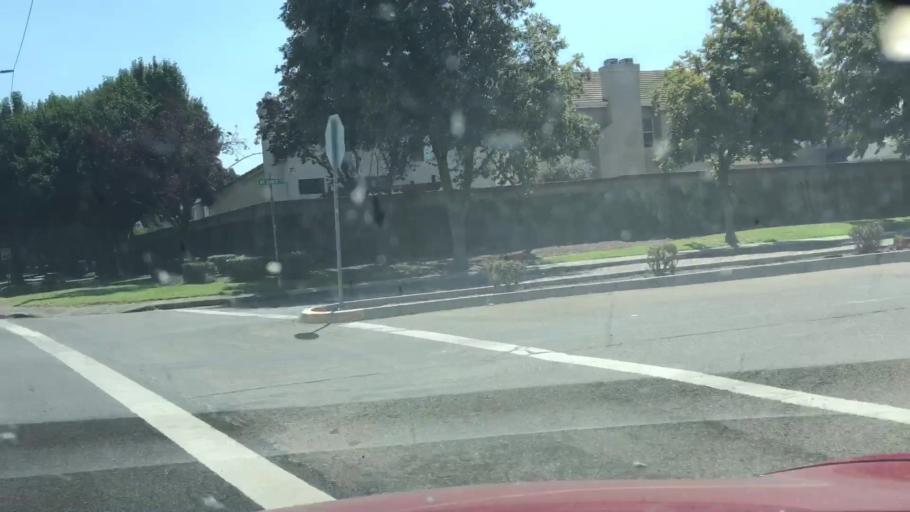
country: US
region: California
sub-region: San Joaquin County
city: Tracy
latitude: 37.7299
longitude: -121.4166
